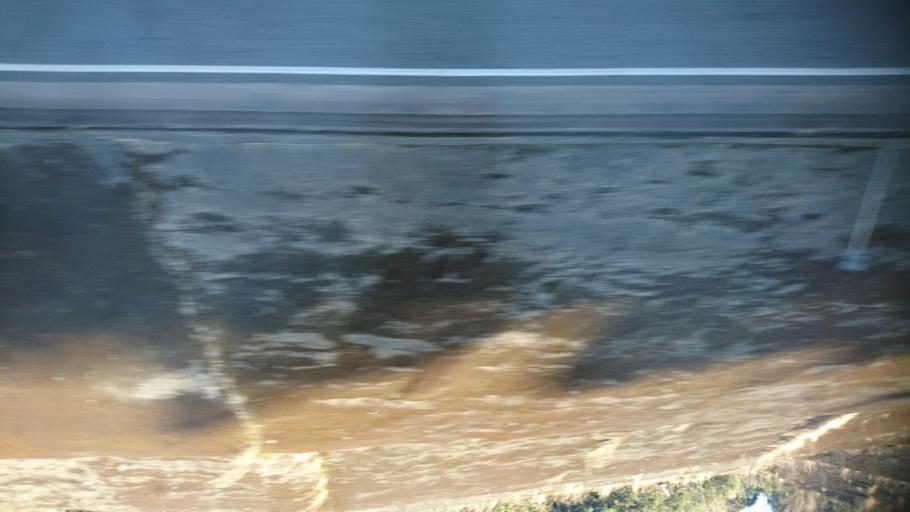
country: JP
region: Miyazaki
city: Miyakonojo
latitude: 31.7952
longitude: 131.1727
